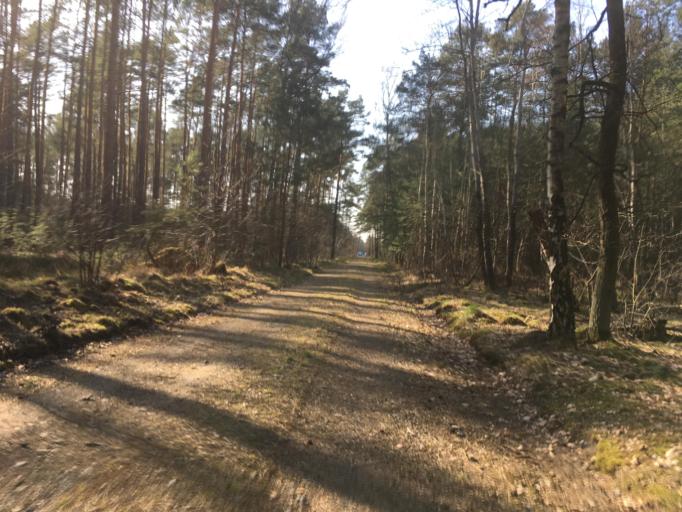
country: DE
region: Brandenburg
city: Wandlitz
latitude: 52.6992
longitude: 13.4454
